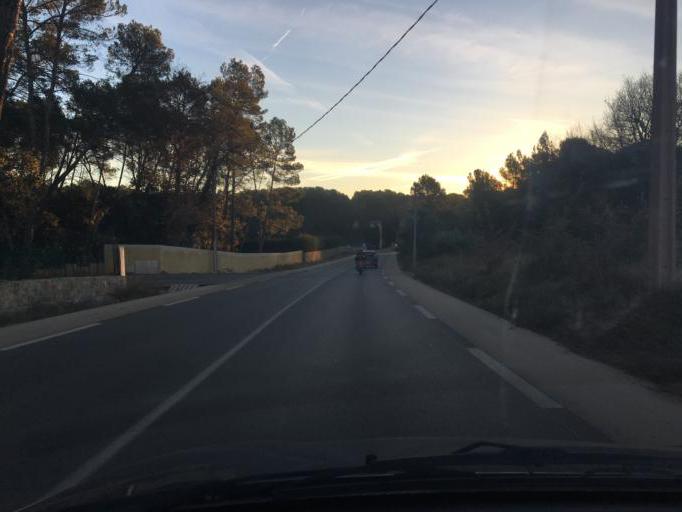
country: FR
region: Provence-Alpes-Cote d'Azur
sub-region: Departement du Var
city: Taradeau
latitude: 43.4647
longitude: 6.3971
